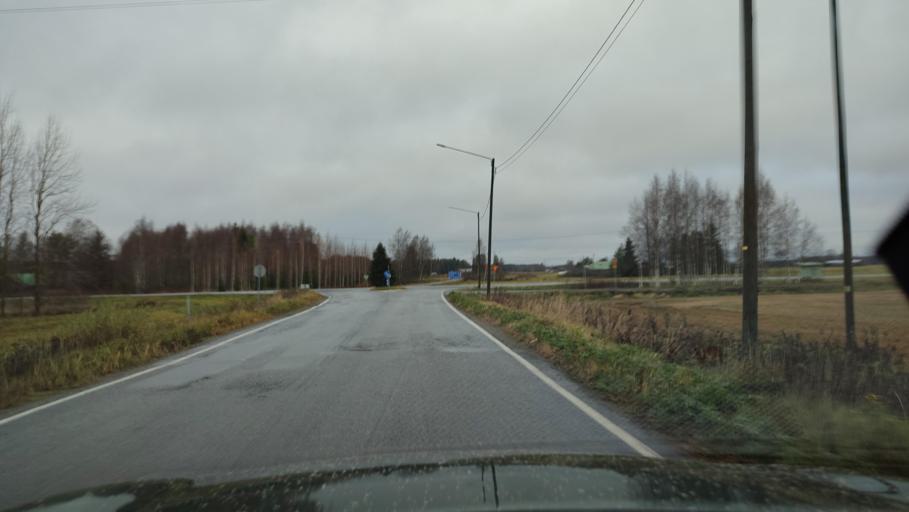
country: FI
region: Southern Ostrobothnia
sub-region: Suupohja
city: Teuva
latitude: 62.4600
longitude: 21.6042
